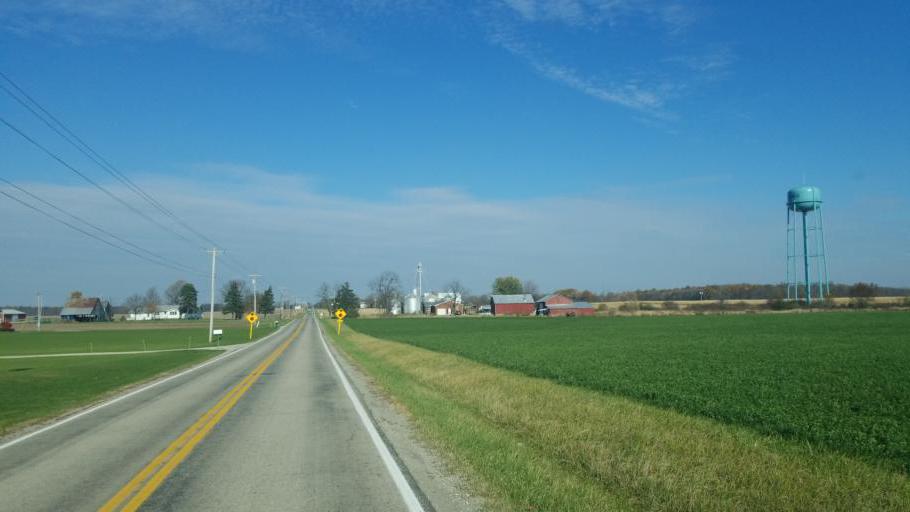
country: US
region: Ohio
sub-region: Lorain County
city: Camden
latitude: 41.2343
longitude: -82.2562
